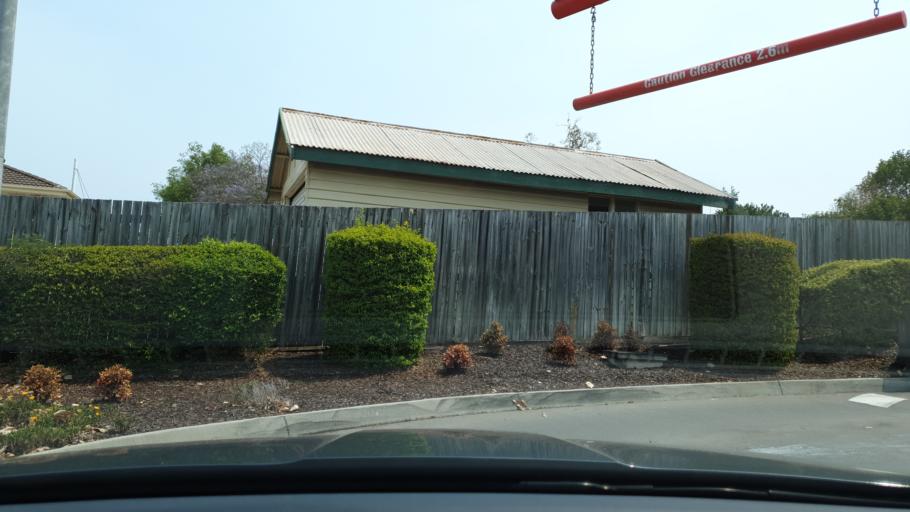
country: AU
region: Queensland
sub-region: Ipswich
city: Booval
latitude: -27.6131
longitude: 152.7993
